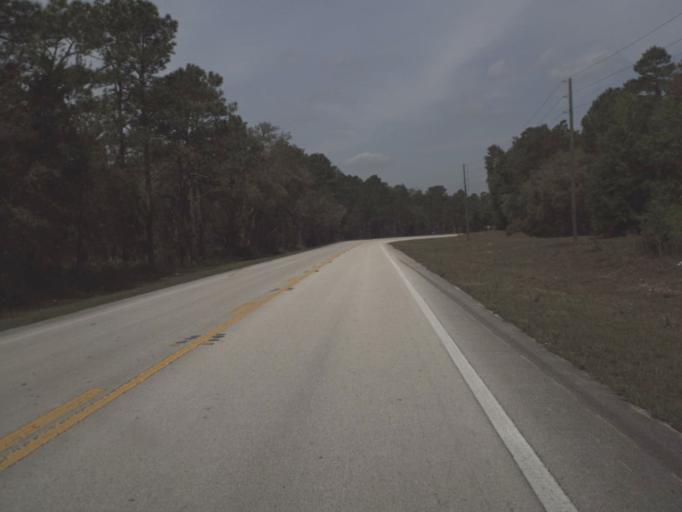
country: US
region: Florida
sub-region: Putnam County
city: Crescent City
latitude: 29.3408
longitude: -81.7315
